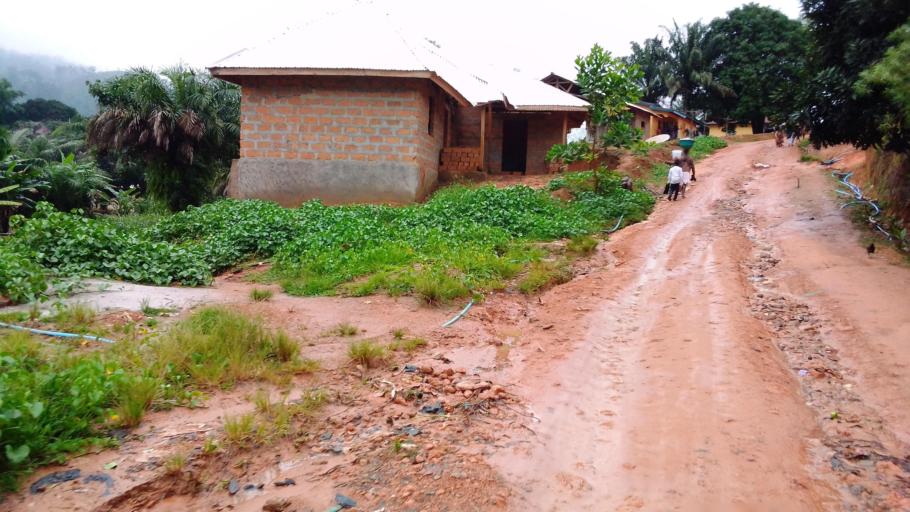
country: SL
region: Eastern Province
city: Kenema
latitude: 7.8965
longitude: -11.1860
